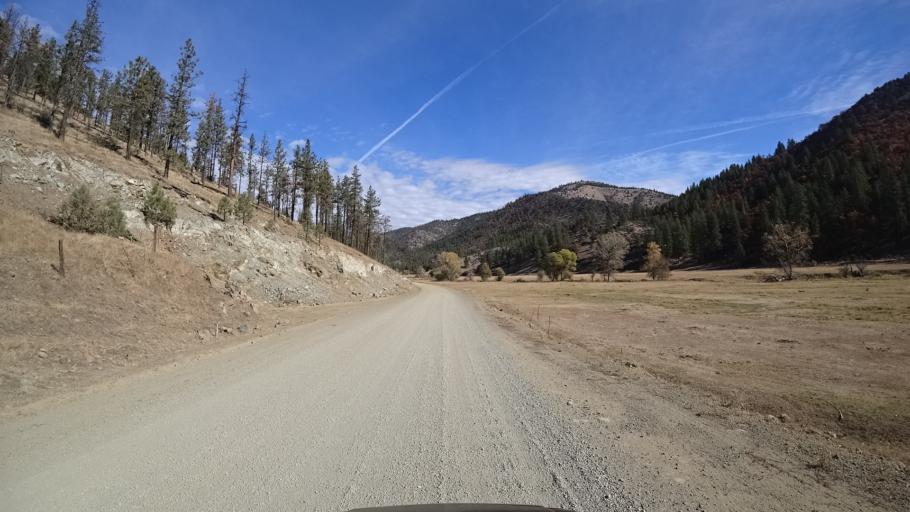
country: US
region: California
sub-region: Siskiyou County
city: Yreka
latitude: 41.6154
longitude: -122.7214
